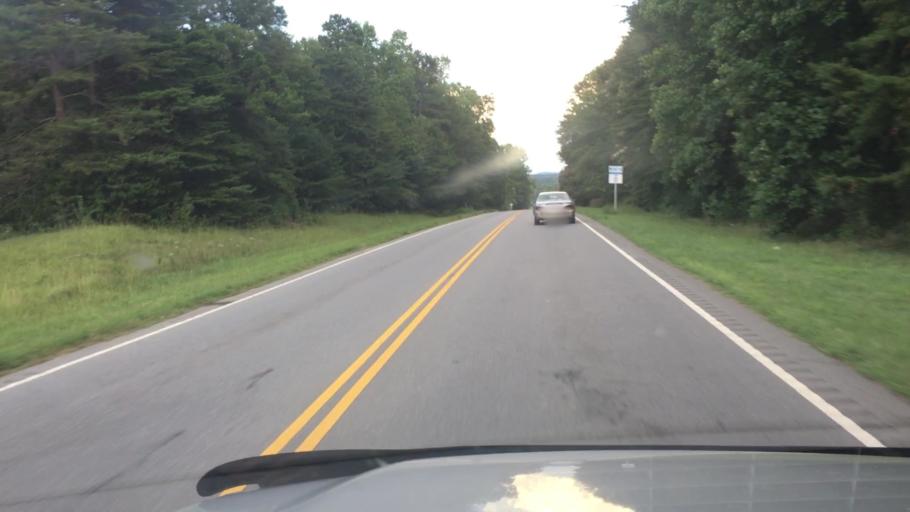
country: US
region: South Carolina
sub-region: Cherokee County
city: Gaffney
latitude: 35.1288
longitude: -81.7378
